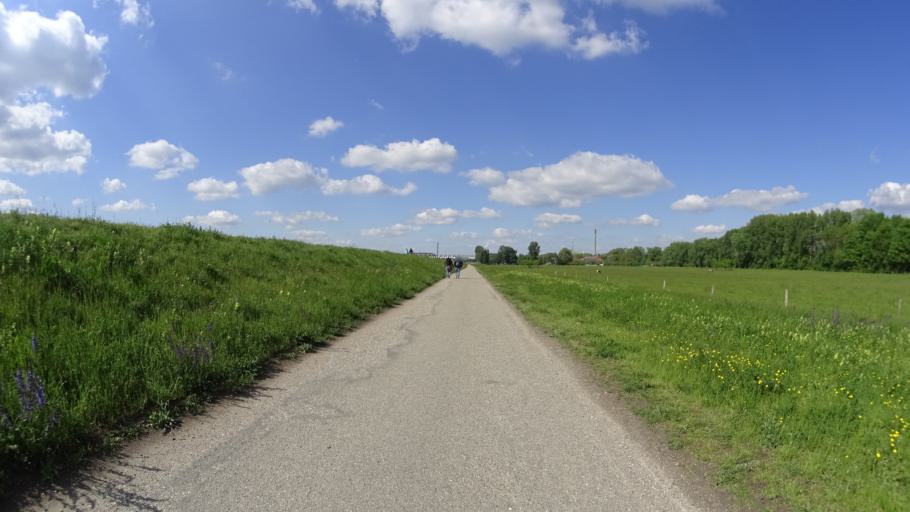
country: DE
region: Rheinland-Pfalz
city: Worth am Rhein
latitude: 49.0267
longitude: 8.3034
